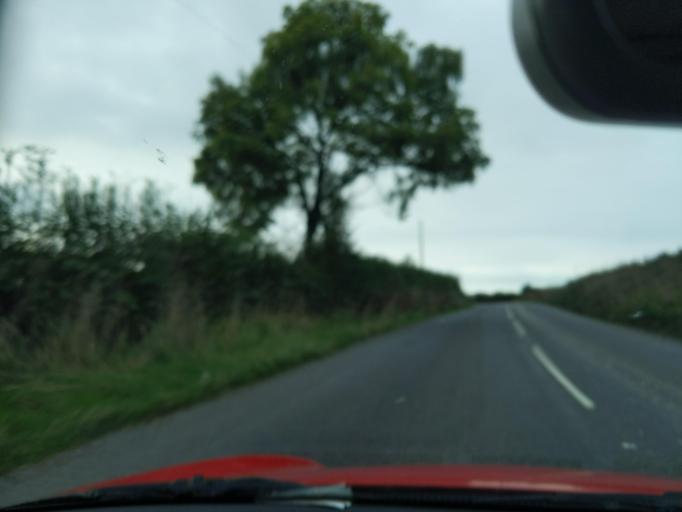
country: GB
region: England
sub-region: Devon
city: Great Torrington
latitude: 50.9114
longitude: -4.1232
